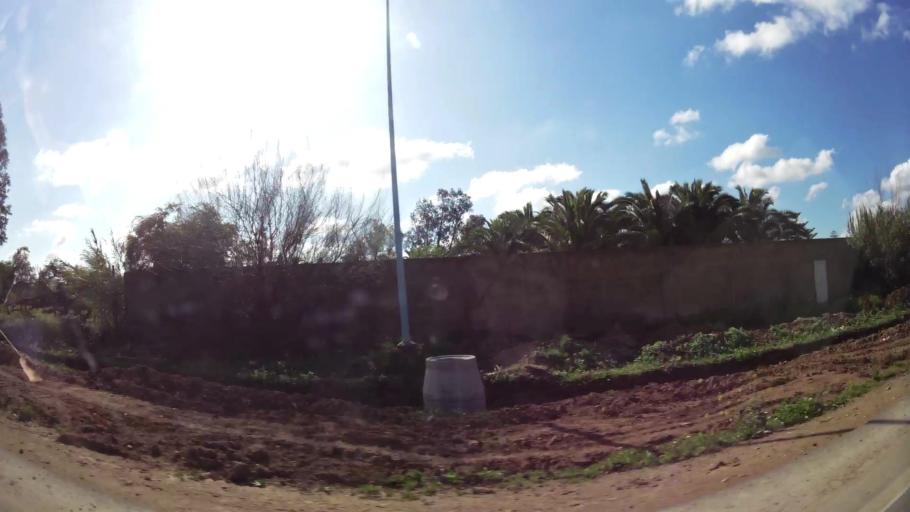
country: MA
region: Grand Casablanca
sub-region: Mediouna
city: Mediouna
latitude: 33.3796
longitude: -7.5406
